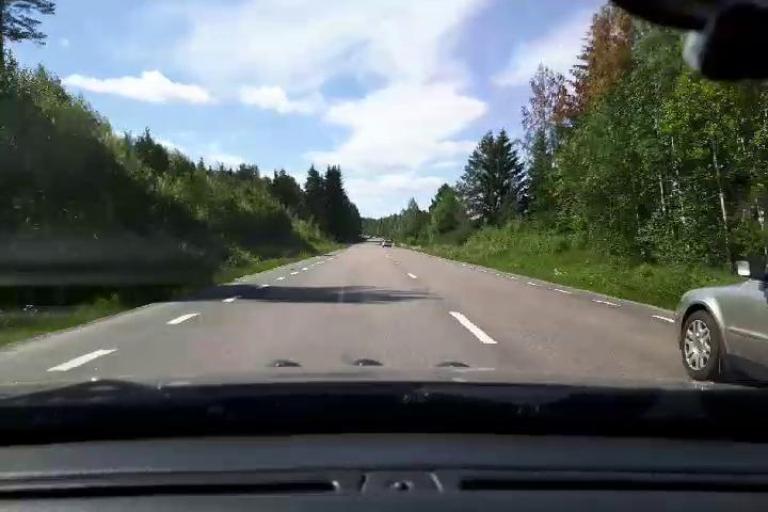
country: SE
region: Gaevleborg
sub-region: Bollnas Kommun
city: Kilafors
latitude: 61.2936
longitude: 16.4965
